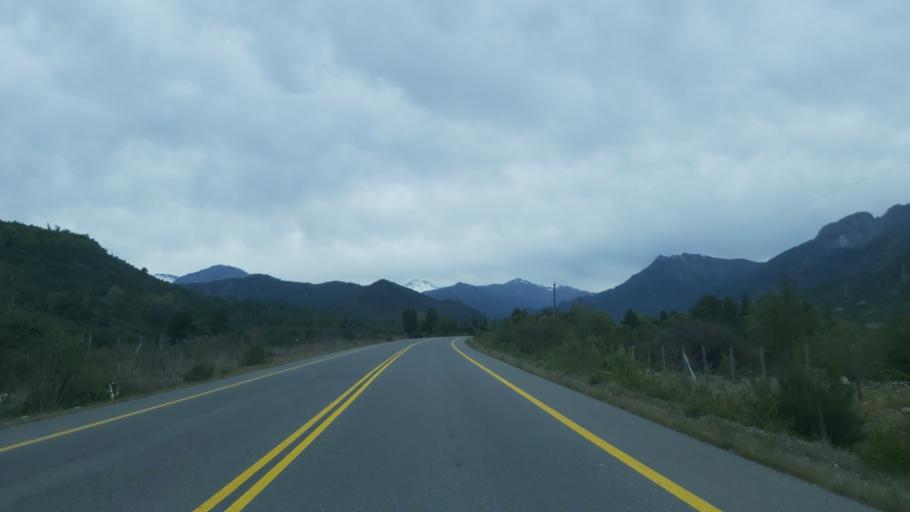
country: CL
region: Maule
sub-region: Provincia de Linares
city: Colbun
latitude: -35.7405
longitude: -71.0094
